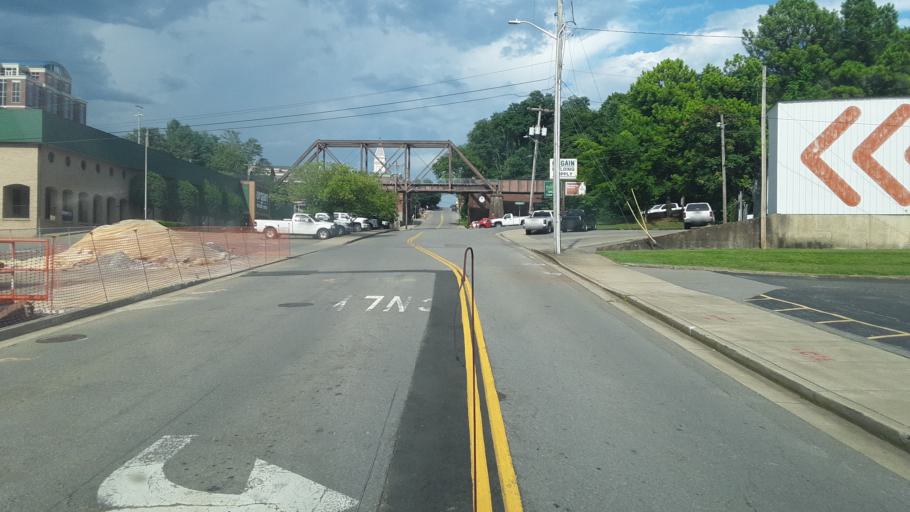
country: US
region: Tennessee
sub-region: Montgomery County
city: Clarksville
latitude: 36.5253
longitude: -87.3632
